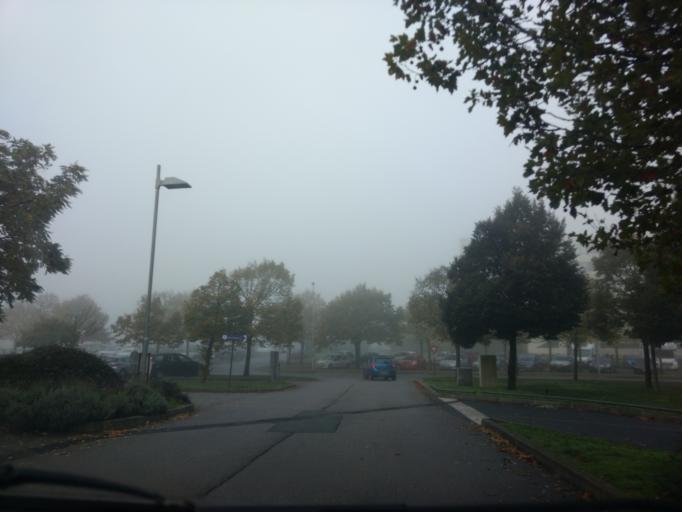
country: FR
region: Poitou-Charentes
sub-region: Departement de la Vienne
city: Chasseneuil-du-Poitou
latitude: 46.6589
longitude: 0.3651
